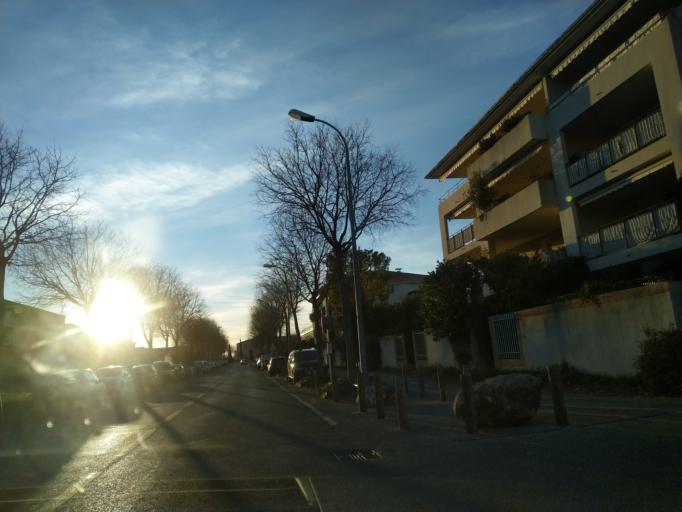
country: FR
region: Provence-Alpes-Cote d'Azur
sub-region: Departement des Bouches-du-Rhone
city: Plan-de-Cuques
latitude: 43.3377
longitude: 5.4466
